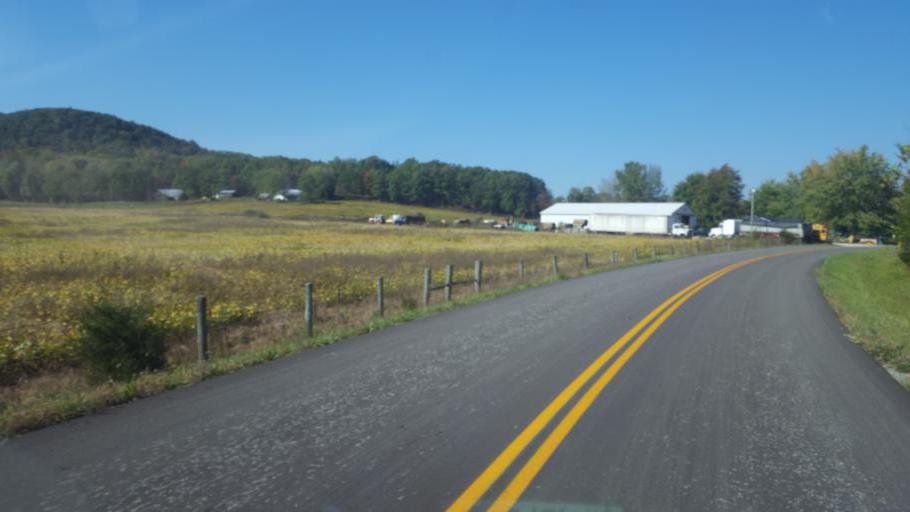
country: US
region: Kentucky
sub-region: Fleming County
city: Flemingsburg
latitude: 38.4479
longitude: -83.5829
